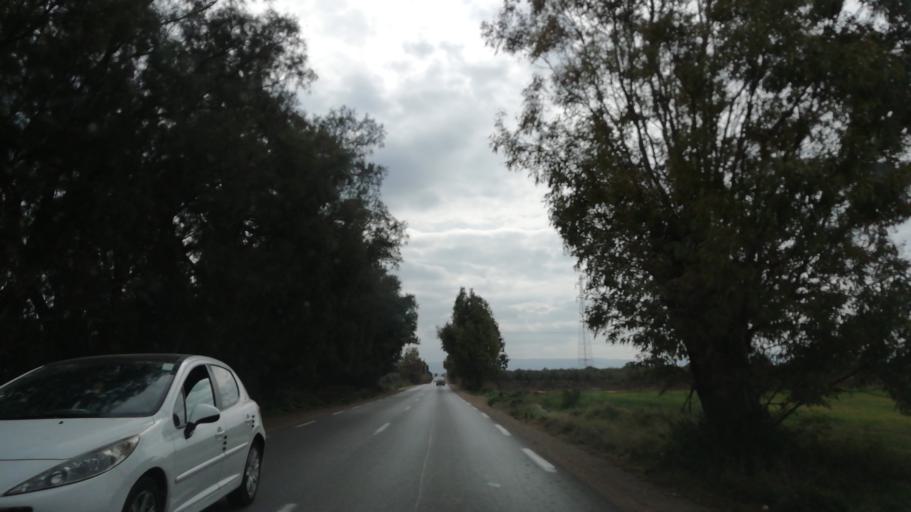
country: DZ
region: Oran
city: Sidi ech Chahmi
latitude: 35.5758
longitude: -0.4515
